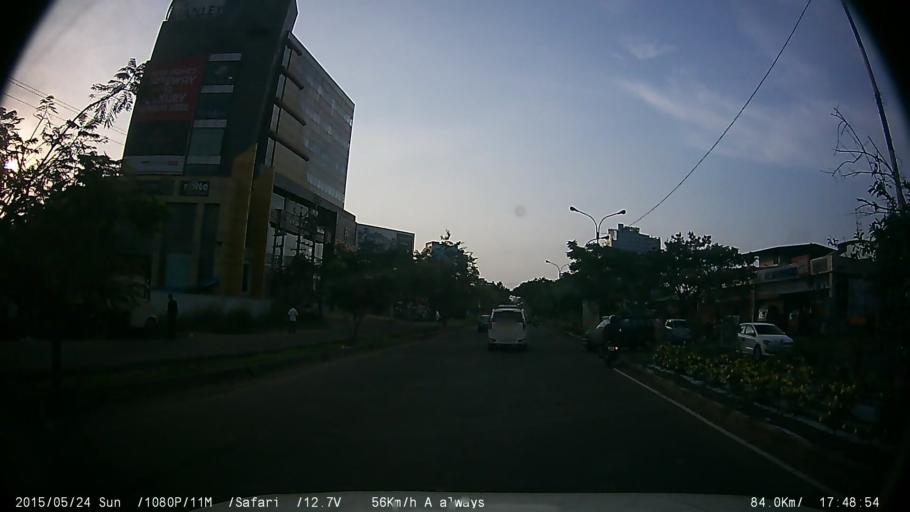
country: IN
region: Kerala
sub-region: Ernakulam
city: Cochin
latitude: 9.9863
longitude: 76.3161
